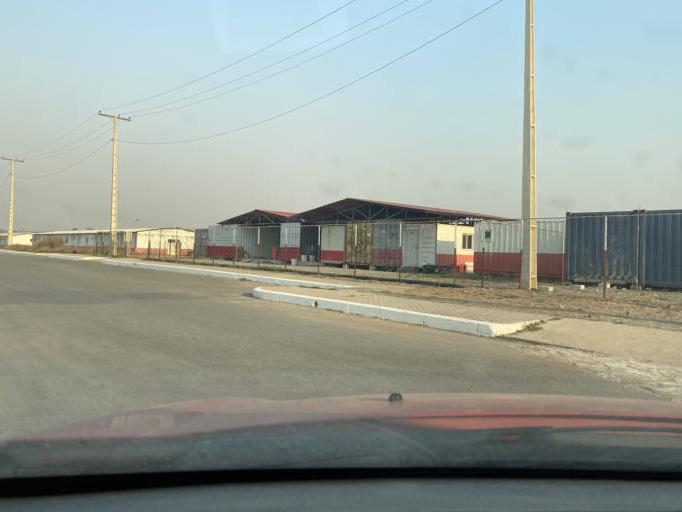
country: AO
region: Cuanza Norte
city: N'dalatando
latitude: -9.7424
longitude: 15.1397
